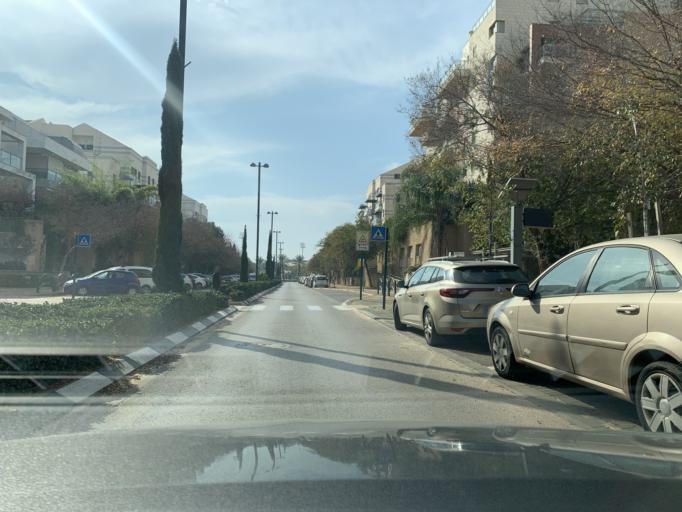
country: IL
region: Central District
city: Kfar Saba
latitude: 32.1866
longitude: 34.9285
